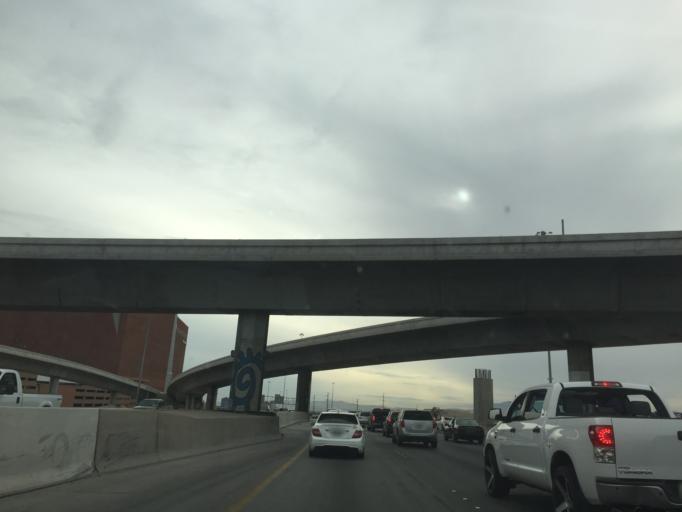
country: US
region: Nevada
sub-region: Clark County
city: Las Vegas
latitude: 36.1731
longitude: -115.1561
